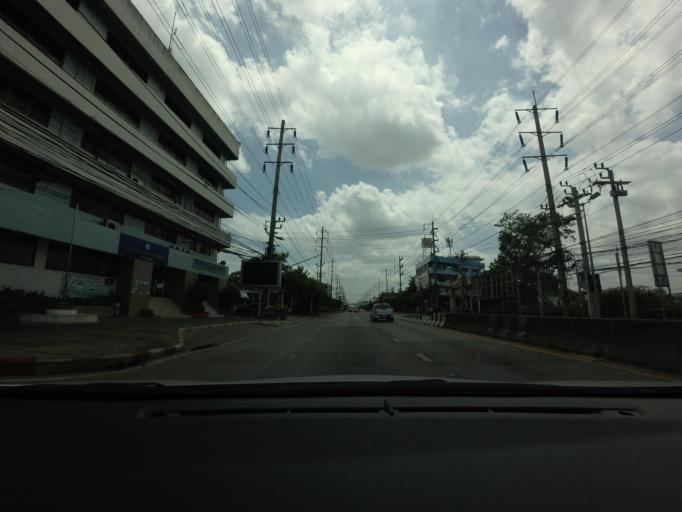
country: TH
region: Samut Prakan
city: Phra Pradaeng
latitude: 13.6468
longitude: 100.5749
